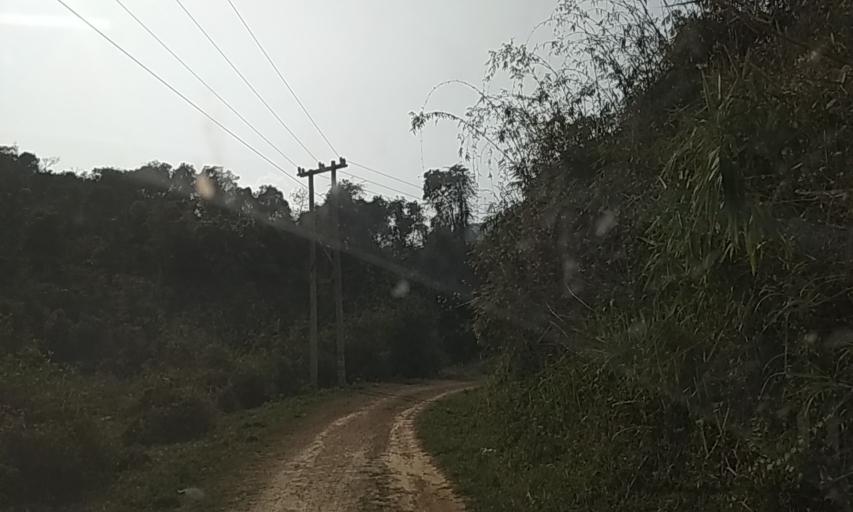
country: LA
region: Louangphabang
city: Louangphabang
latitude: 20.0427
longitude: 101.8072
